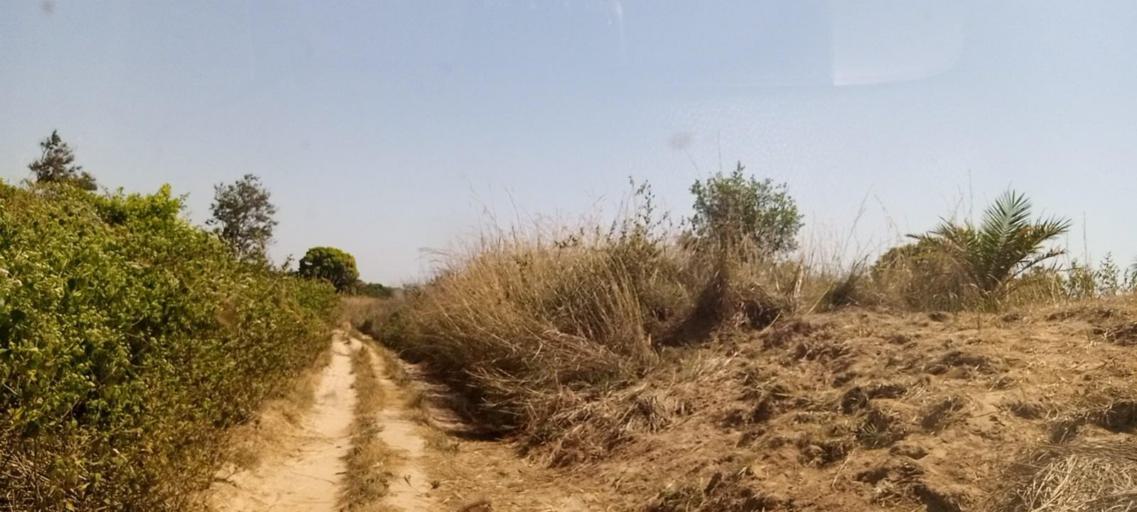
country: CD
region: Kasai-Oriental
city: Kabinda
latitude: -5.9562
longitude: 24.8003
